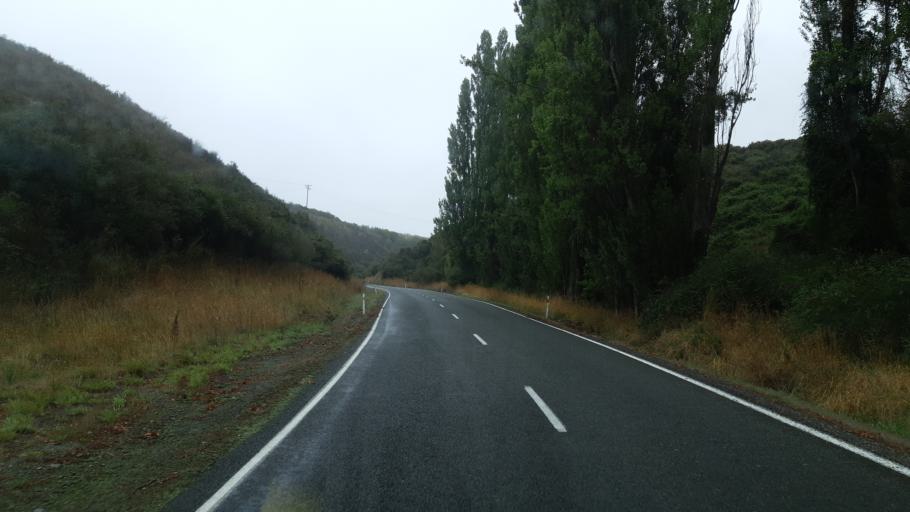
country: NZ
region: Otago
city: Oamaru
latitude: -44.9122
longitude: 170.8416
